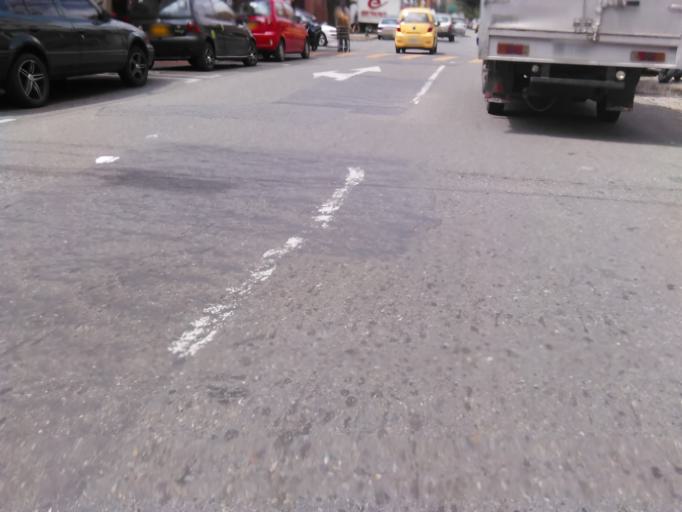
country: CO
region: Antioquia
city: Medellin
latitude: 6.2323
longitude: -75.5933
